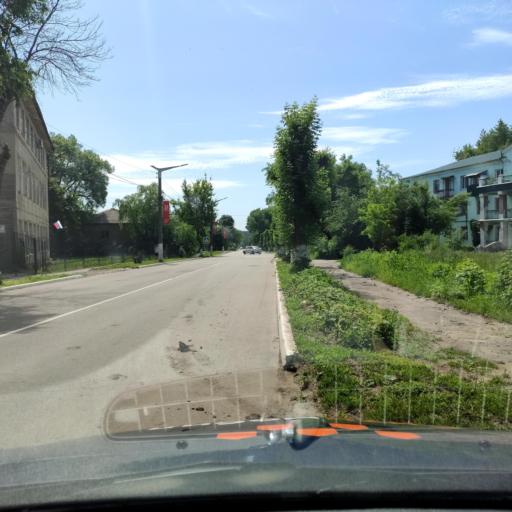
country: RU
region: Voronezj
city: Semiluki
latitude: 51.6863
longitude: 39.0397
